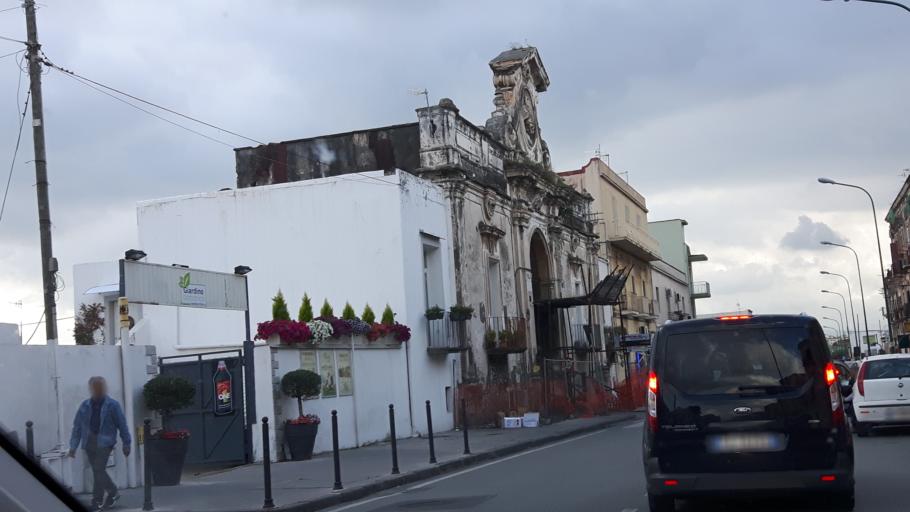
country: IT
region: Campania
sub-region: Provincia di Napoli
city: Torre del Greco
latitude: 40.7671
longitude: 14.4124
